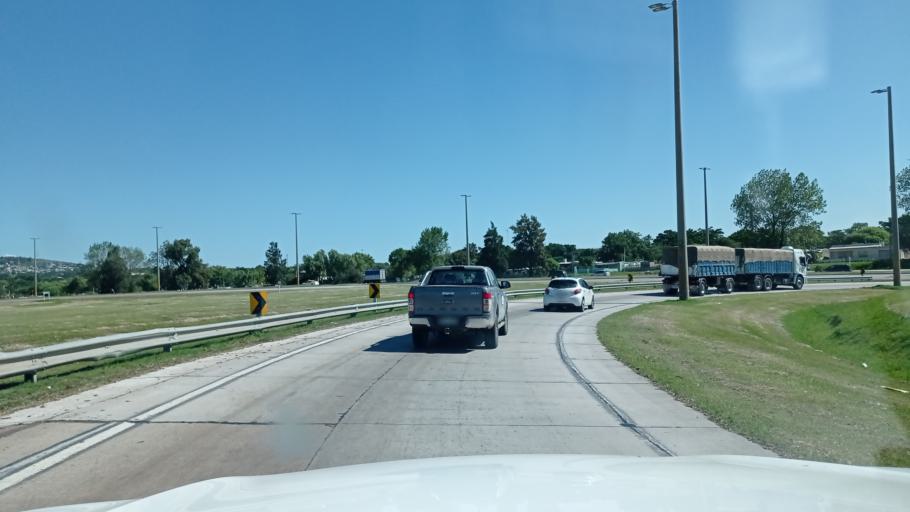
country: UY
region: Montevideo
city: Montevideo
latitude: -34.8598
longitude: -56.2556
